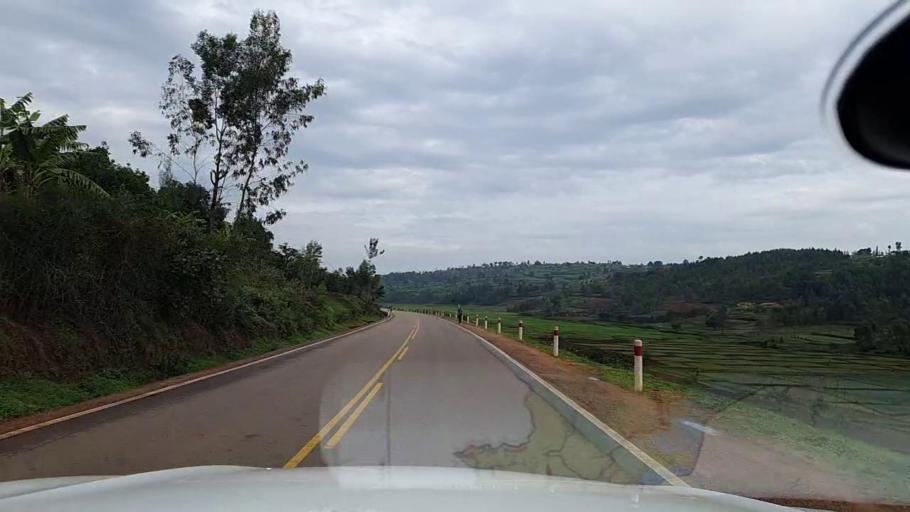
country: RW
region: Southern Province
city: Butare
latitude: -2.5728
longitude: 29.7323
